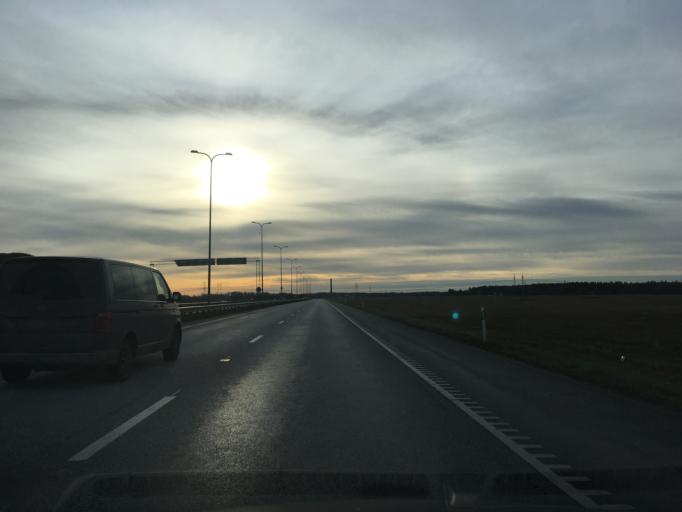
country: EE
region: Ida-Virumaa
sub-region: Kohtla-Jaerve linn
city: Kohtla-Jarve
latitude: 59.3972
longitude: 27.3332
